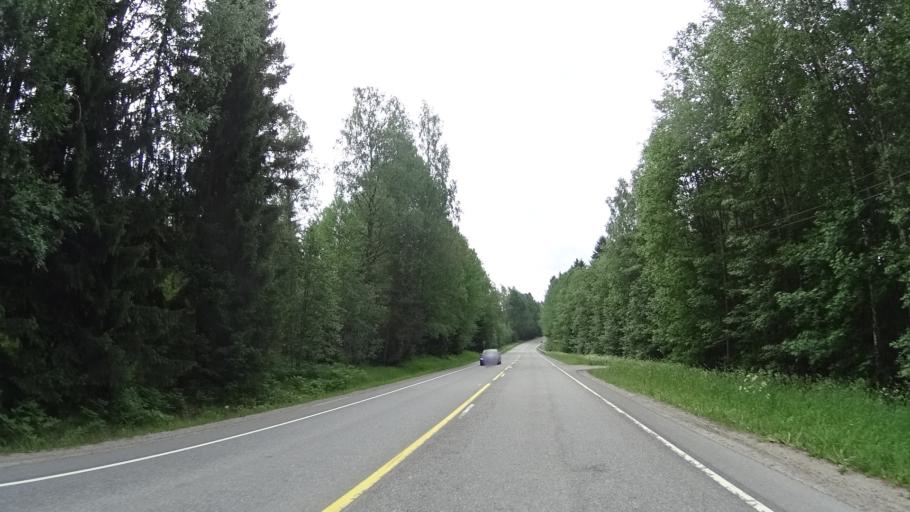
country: FI
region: Uusimaa
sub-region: Helsinki
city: Vihti
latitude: 60.2864
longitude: 24.4067
